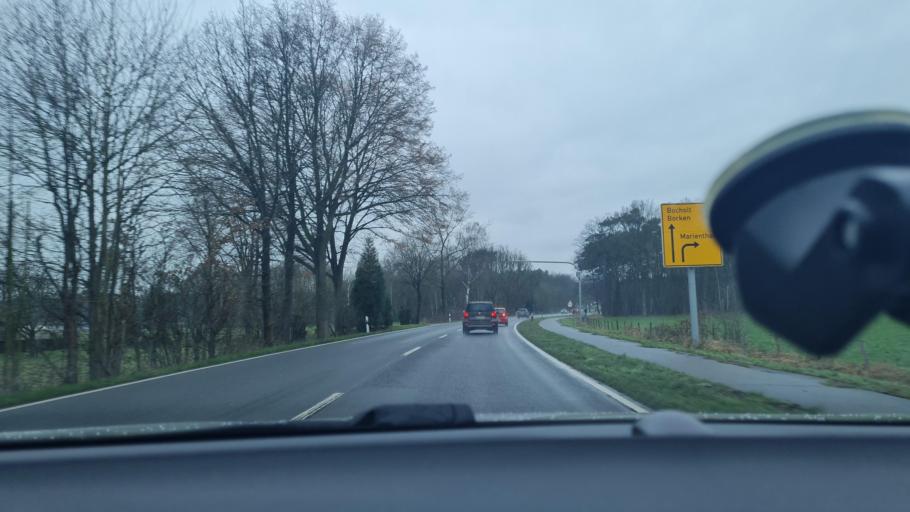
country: DE
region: North Rhine-Westphalia
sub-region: Regierungsbezirk Dusseldorf
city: Hunxe
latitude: 51.6751
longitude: 6.7406
